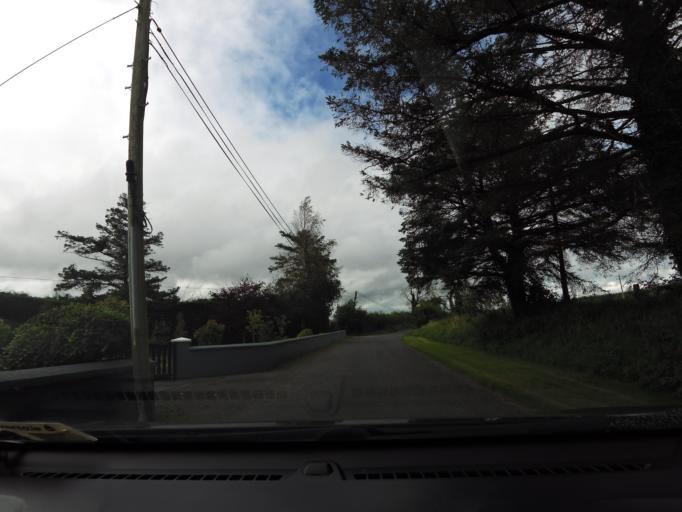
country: IE
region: Connaught
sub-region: County Galway
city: Loughrea
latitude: 53.2994
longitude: -8.5976
